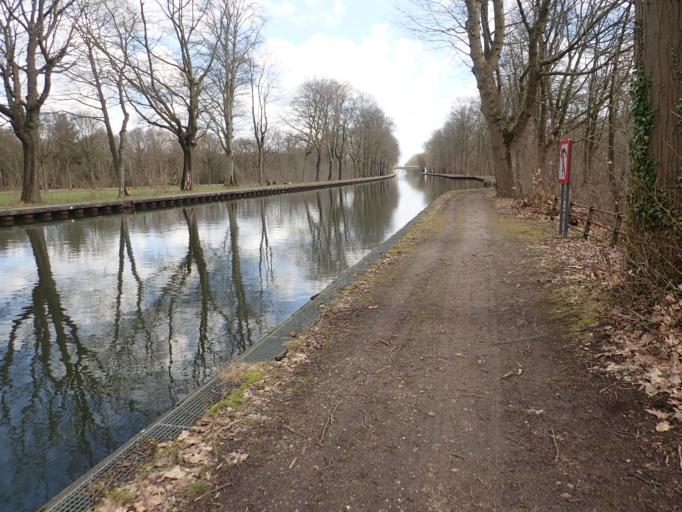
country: BE
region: Flanders
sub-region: Provincie Antwerpen
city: Vosselaar
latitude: 51.3280
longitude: 4.9045
